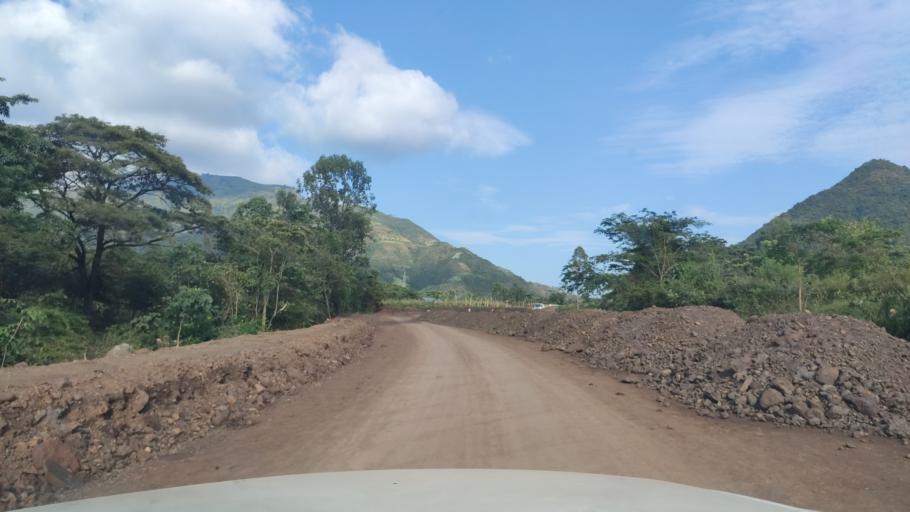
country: ET
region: Southern Nations, Nationalities, and People's Region
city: Arba Minch'
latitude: 6.4261
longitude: 37.3310
